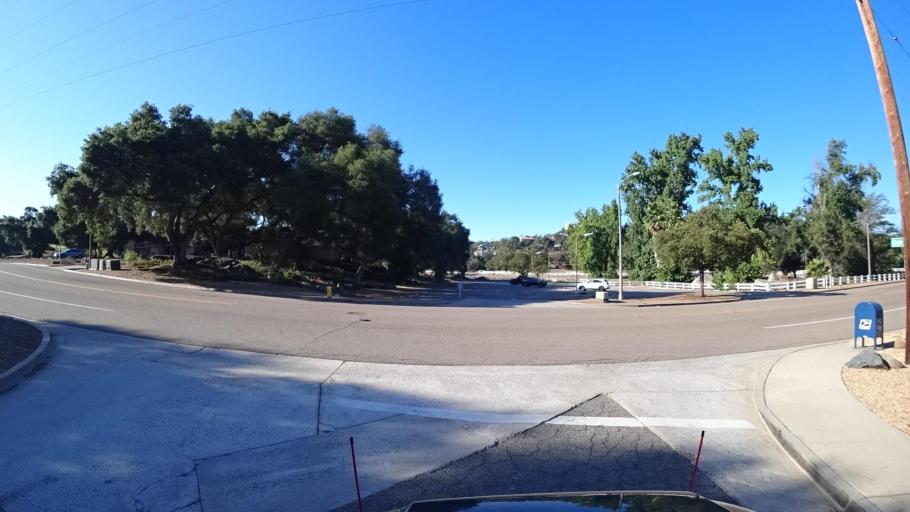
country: US
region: California
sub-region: San Diego County
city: Hidden Meadows
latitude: 33.2157
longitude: -117.1091
